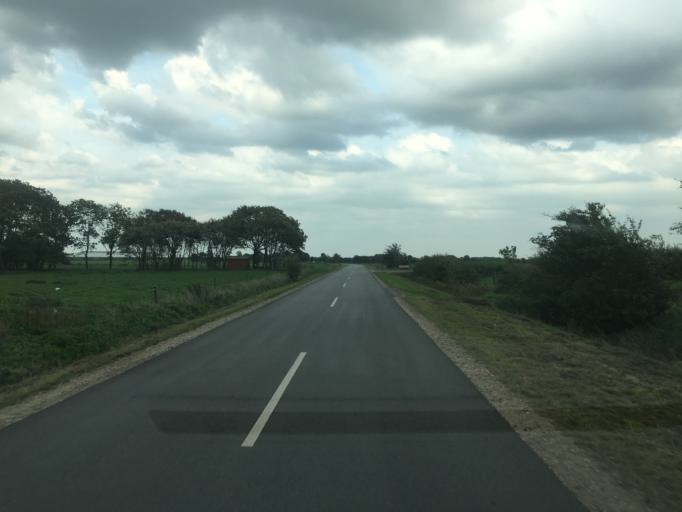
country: DK
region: South Denmark
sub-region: Tonder Kommune
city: Logumkloster
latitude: 55.0613
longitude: 9.0475
